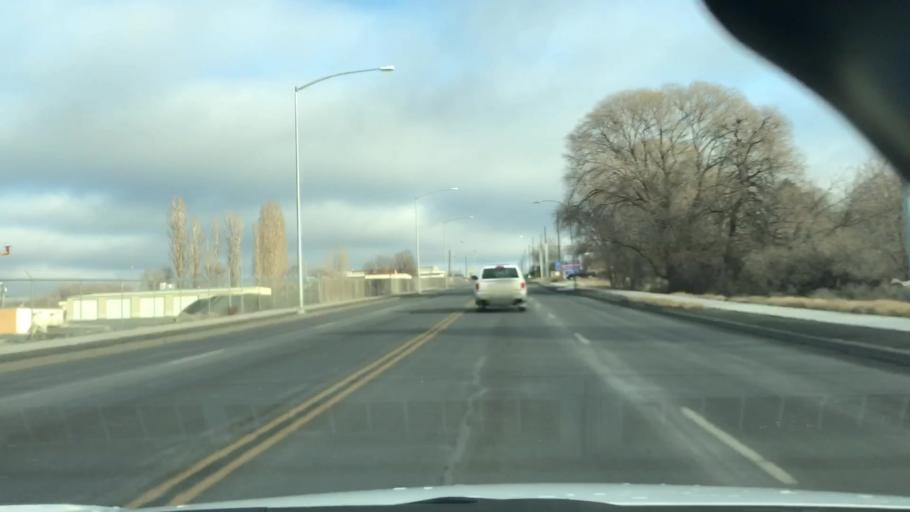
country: US
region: Washington
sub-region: Grant County
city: Moses Lake
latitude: 47.1311
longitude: -119.2666
